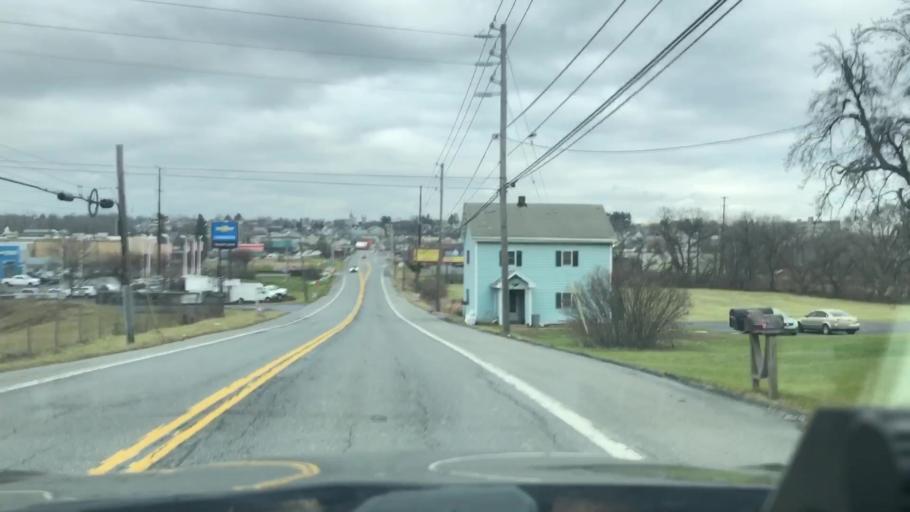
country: US
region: Pennsylvania
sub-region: Northampton County
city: Nazareth
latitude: 40.7276
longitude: -75.3156
